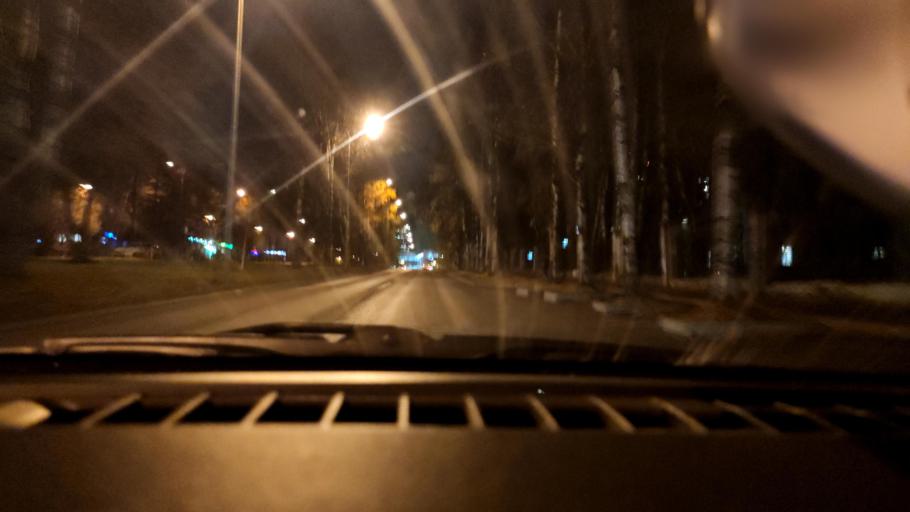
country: RU
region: Perm
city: Perm
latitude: 57.9801
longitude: 56.1822
